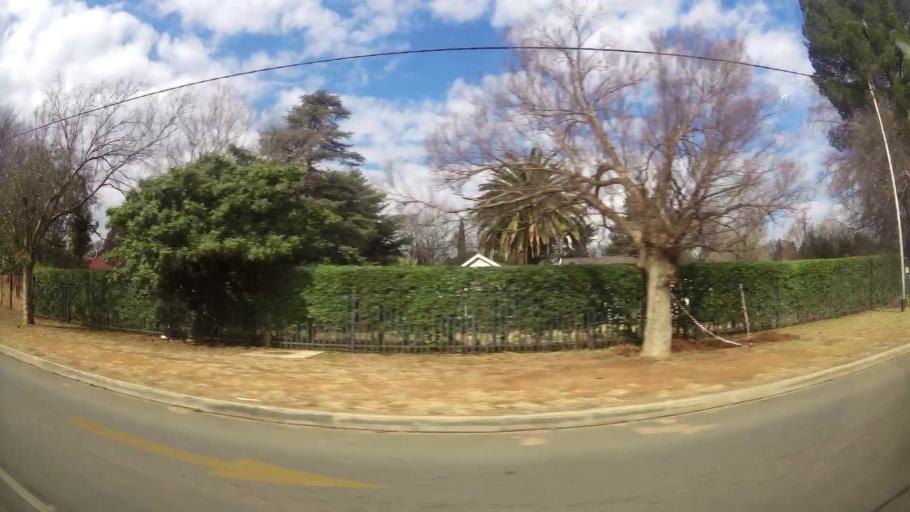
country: ZA
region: Gauteng
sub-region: Sedibeng District Municipality
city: Vereeniging
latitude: -26.6591
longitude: 27.9869
